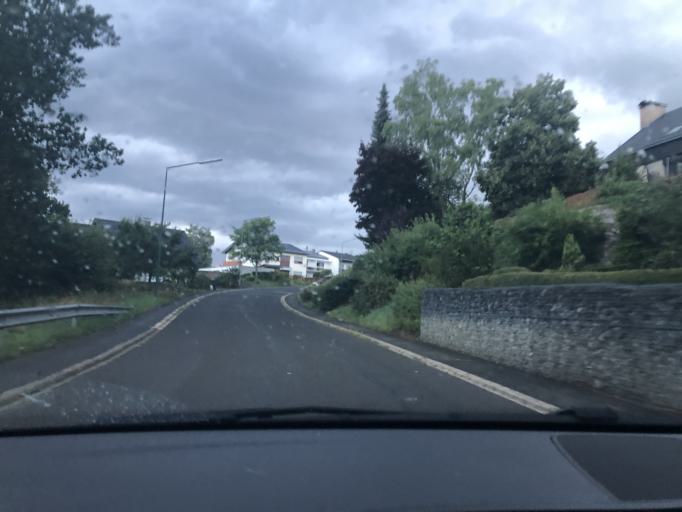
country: DE
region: Rheinland-Pfalz
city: Hermeskeil
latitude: 49.6585
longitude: 6.9406
